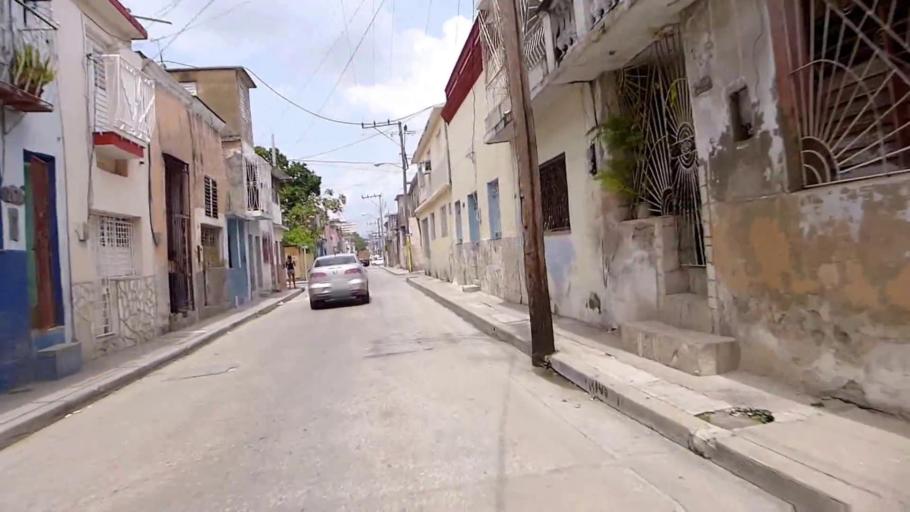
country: CU
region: Holguin
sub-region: Municipio de Holguin
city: Holguin
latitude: 20.8899
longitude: -76.2633
